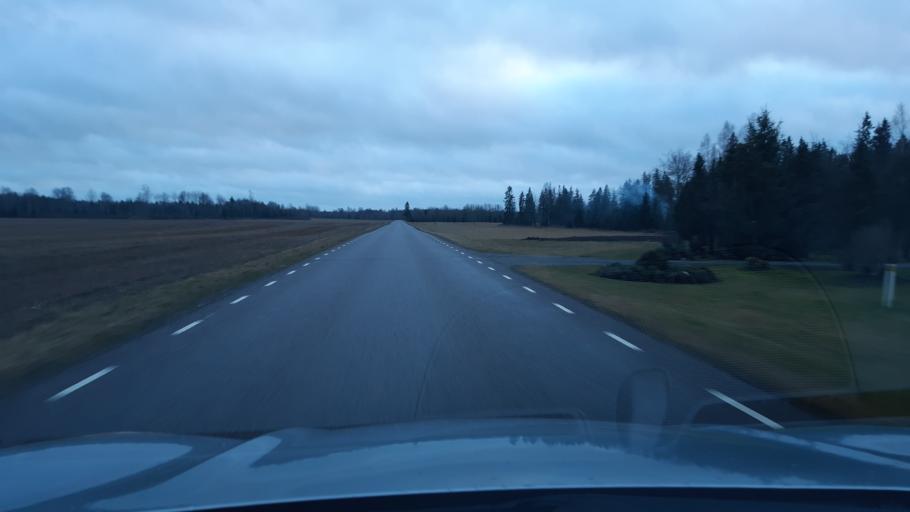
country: EE
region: Raplamaa
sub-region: Kohila vald
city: Kohila
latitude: 59.0972
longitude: 24.6733
